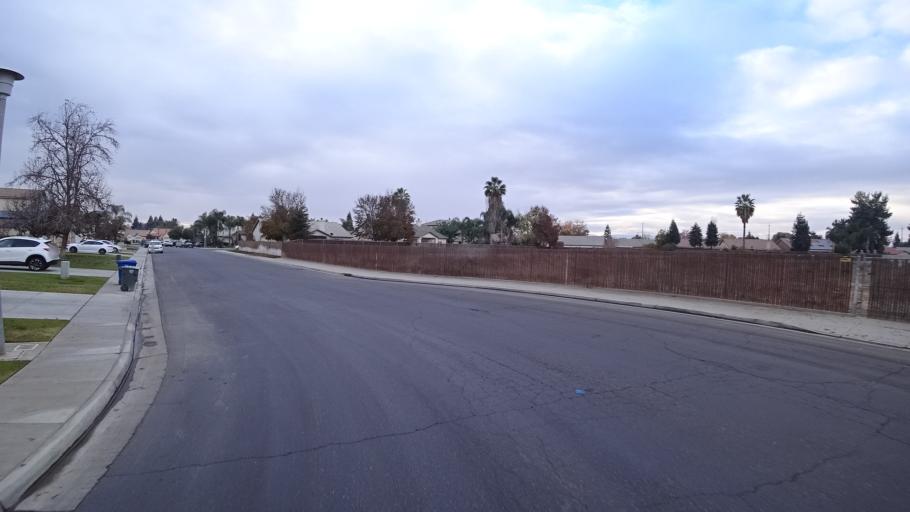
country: US
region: California
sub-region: Kern County
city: Greenfield
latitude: 35.2987
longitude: -119.0823
